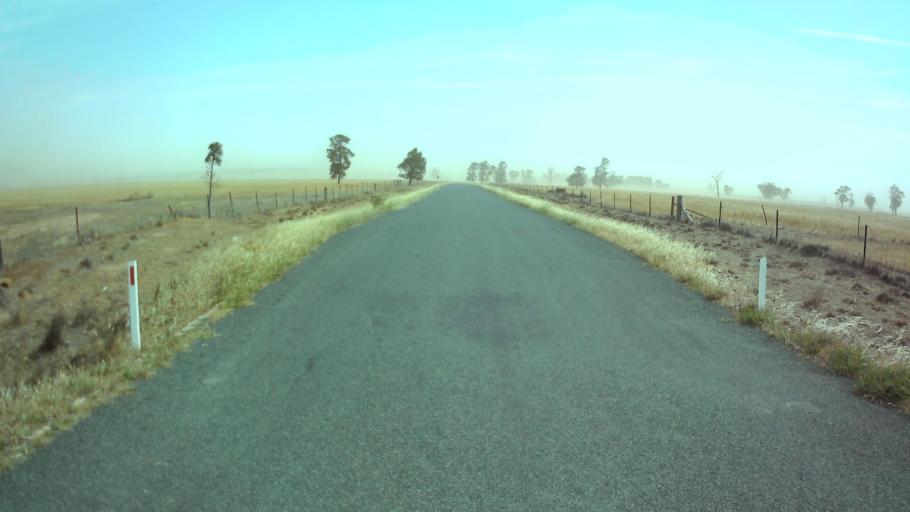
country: AU
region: New South Wales
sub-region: Weddin
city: Grenfell
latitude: -33.7407
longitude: 147.9927
